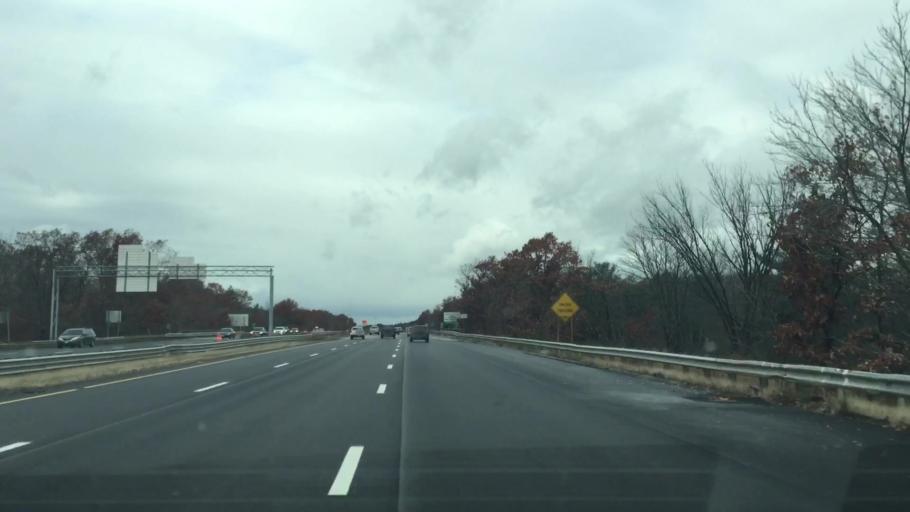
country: US
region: Massachusetts
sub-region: Essex County
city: Methuen
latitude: 42.7419
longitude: -71.2082
